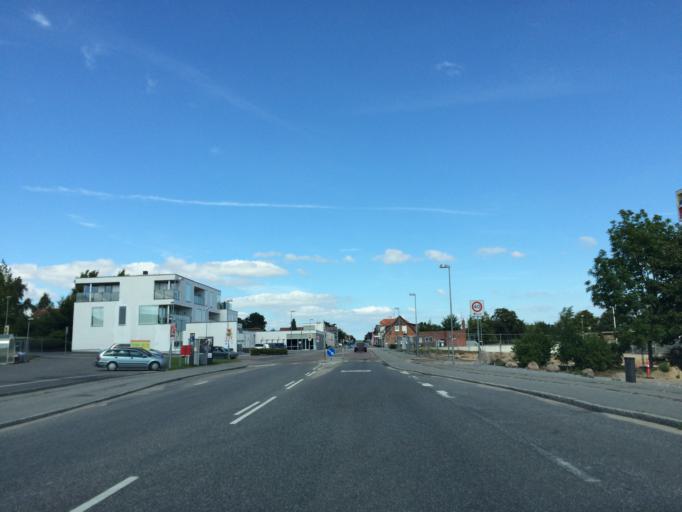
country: DK
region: Central Jutland
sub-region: Arhus Kommune
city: Logten
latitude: 56.2757
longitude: 10.3151
